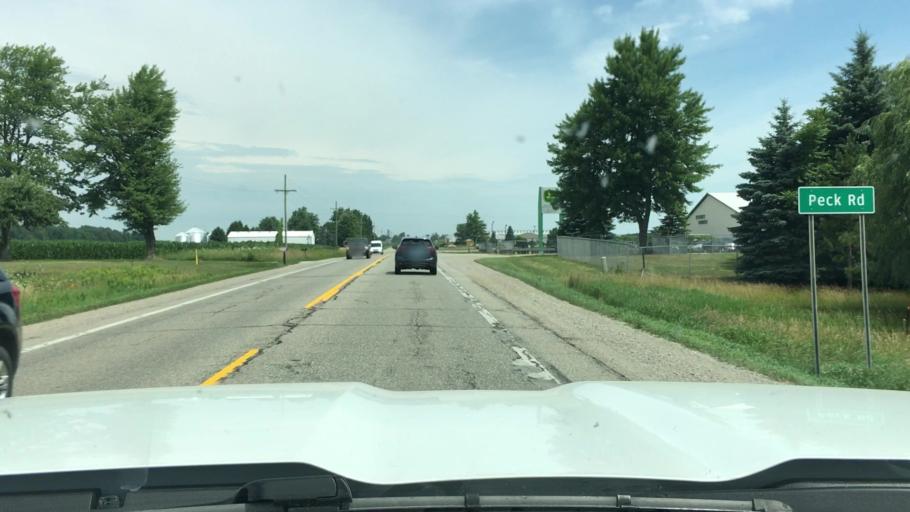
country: US
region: Michigan
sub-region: Sanilac County
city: Marlette
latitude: 43.2530
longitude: -83.0793
